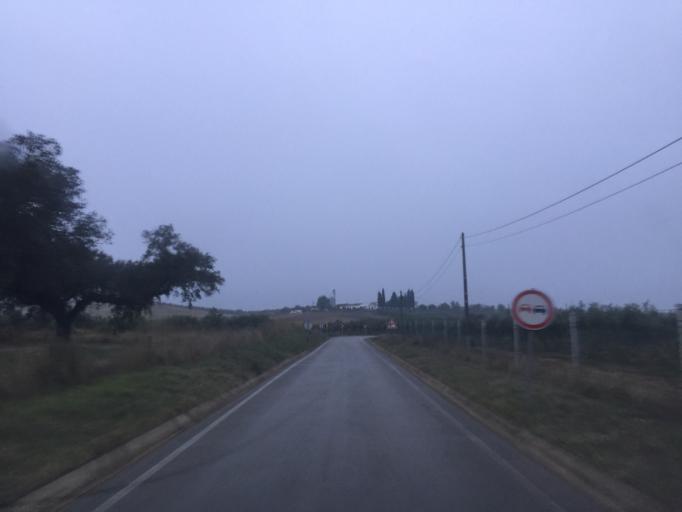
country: PT
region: Portalegre
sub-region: Avis
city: Avis
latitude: 39.0464
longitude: -7.9066
